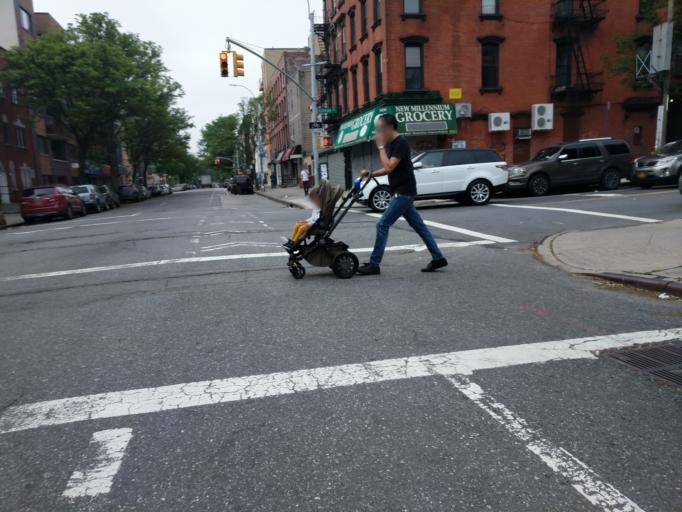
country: US
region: New York
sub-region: Kings County
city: Brooklyn
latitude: 40.6879
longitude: -73.9571
